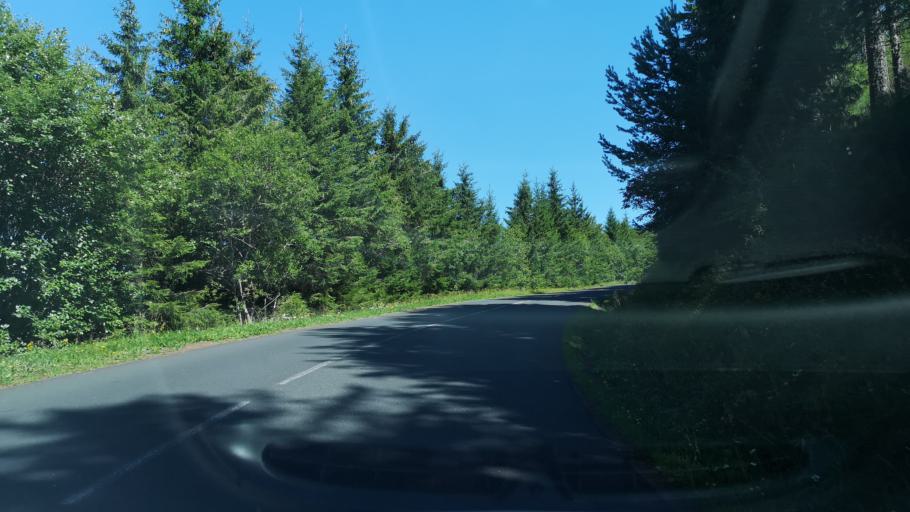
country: FR
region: Auvergne
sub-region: Departement du Puy-de-Dome
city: Mont-Dore
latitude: 45.5919
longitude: 2.8281
